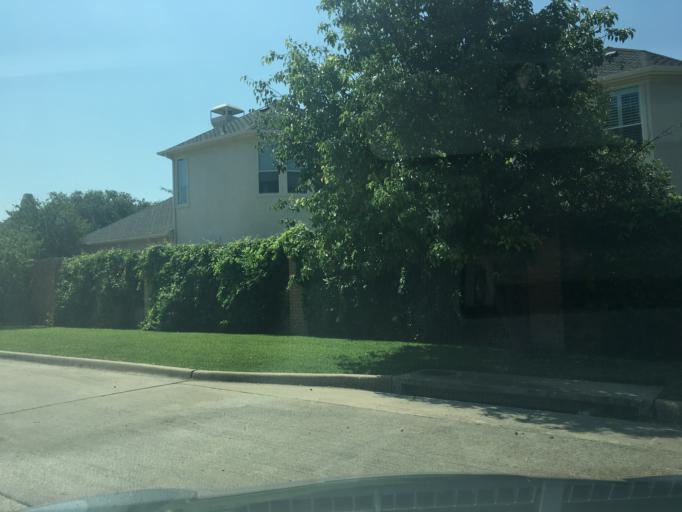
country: US
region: Texas
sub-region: Dallas County
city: Addison
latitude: 32.9127
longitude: -96.7959
